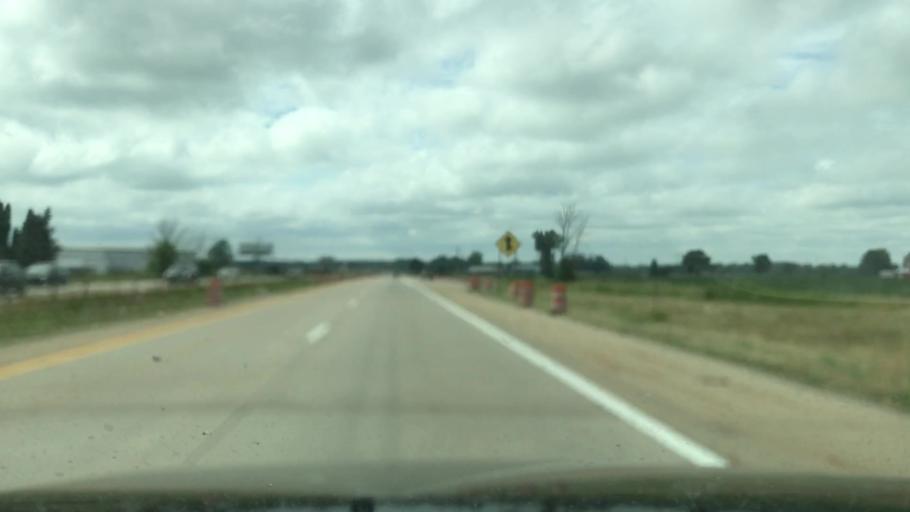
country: US
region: Michigan
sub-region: Ottawa County
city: Coopersville
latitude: 43.0602
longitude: -85.9637
